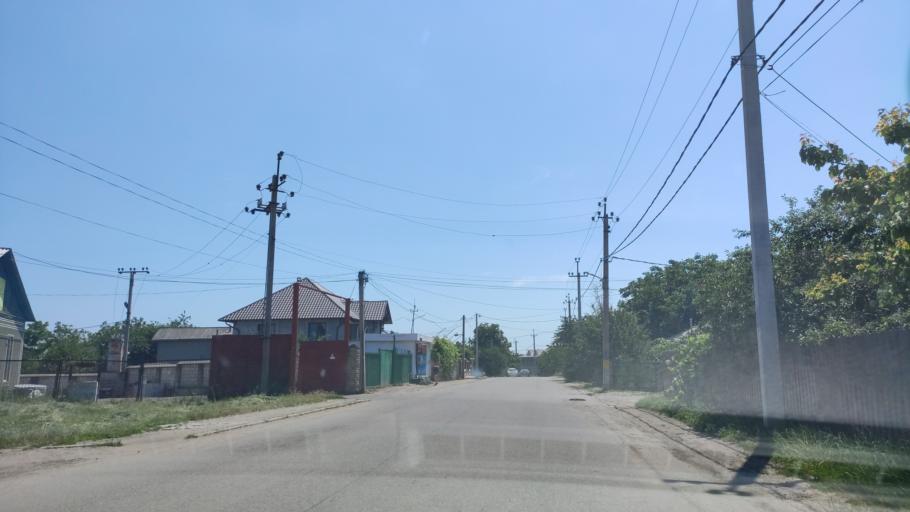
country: MD
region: Raionul Soroca
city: Soroca
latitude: 48.1495
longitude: 28.2790
